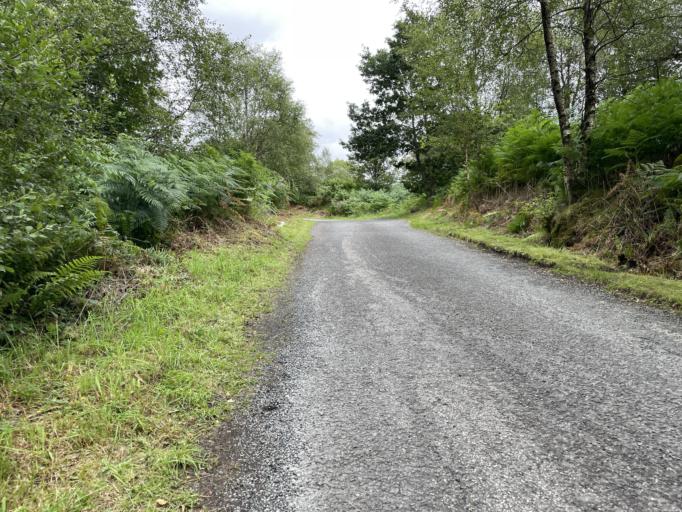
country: GB
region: Scotland
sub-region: Dumfries and Galloway
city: Newton Stewart
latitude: 55.0926
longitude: -4.4848
